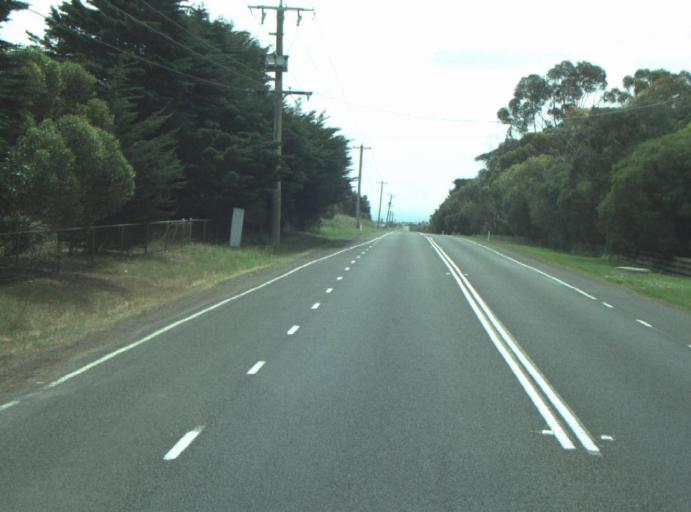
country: AU
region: Victoria
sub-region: Greater Geelong
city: Clifton Springs
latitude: -38.1337
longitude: 144.6162
